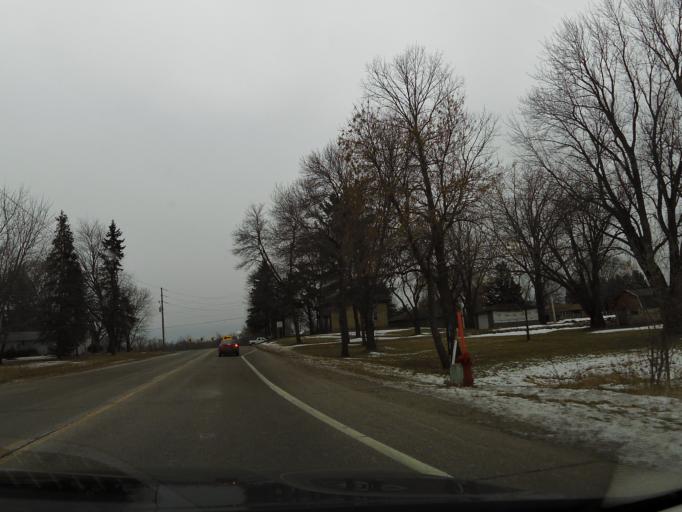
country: US
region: Minnesota
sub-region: Carver County
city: Cologne
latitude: 44.7786
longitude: -93.7881
